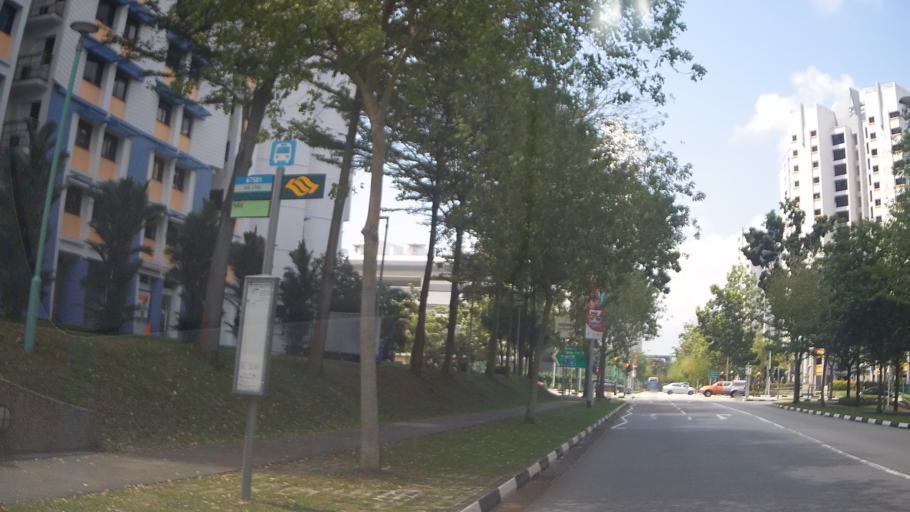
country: MY
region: Johor
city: Kampung Pasir Gudang Baru
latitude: 1.3915
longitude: 103.8899
